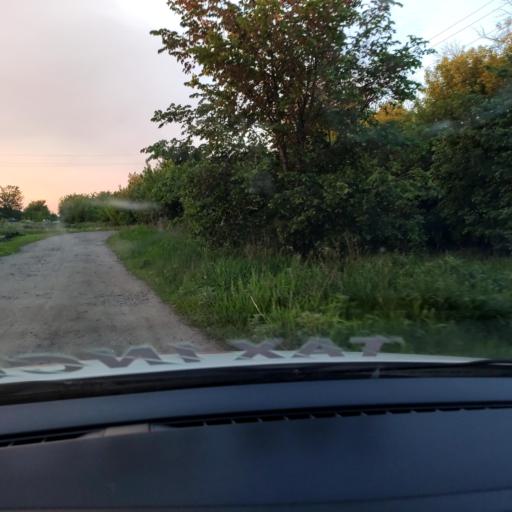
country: RU
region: Voronezj
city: Maslovka
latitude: 51.4561
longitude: 39.2334
